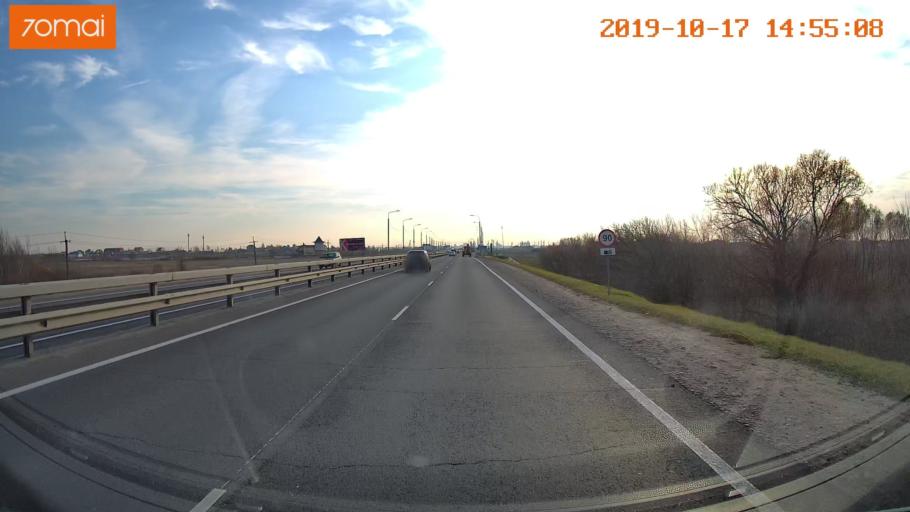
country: RU
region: Rjazan
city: Polyany
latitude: 54.6721
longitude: 39.8272
